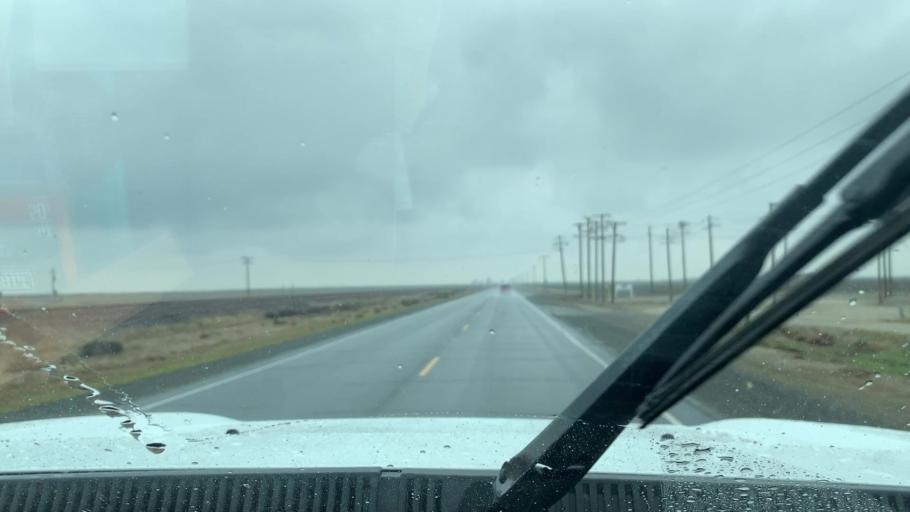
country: US
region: California
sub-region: Tulare County
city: Alpaugh
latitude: 35.9627
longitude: -119.4573
